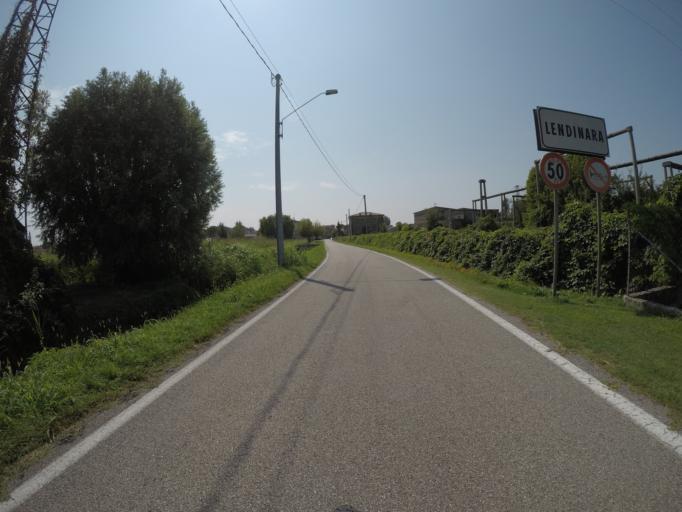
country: IT
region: Veneto
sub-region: Provincia di Rovigo
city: Lendinara
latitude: 45.0906
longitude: 11.5896
